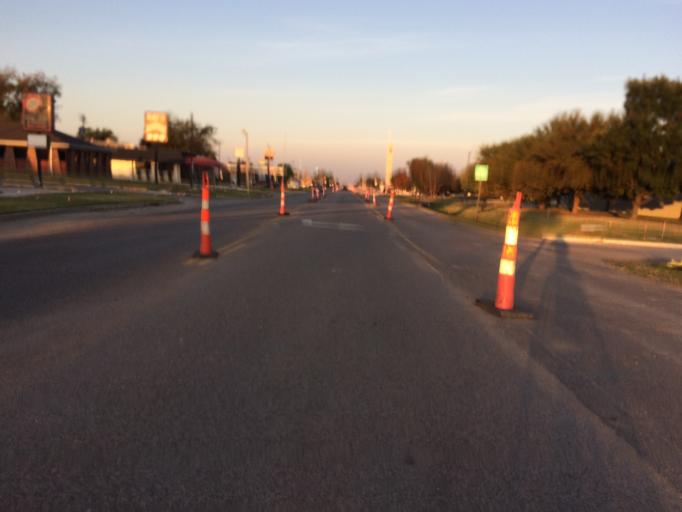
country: US
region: Oklahoma
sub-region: Cleveland County
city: Norman
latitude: 35.2039
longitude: -97.4634
